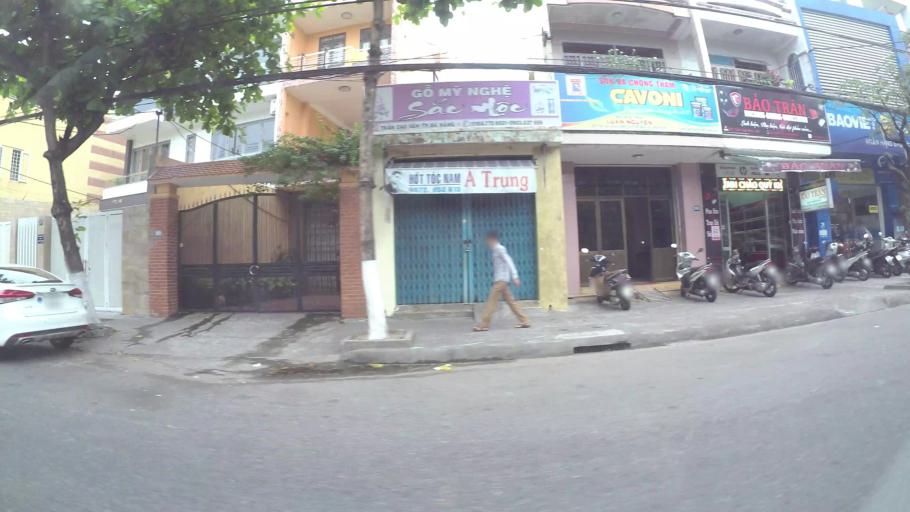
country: VN
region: Da Nang
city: Thanh Khe
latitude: 16.0711
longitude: 108.1975
